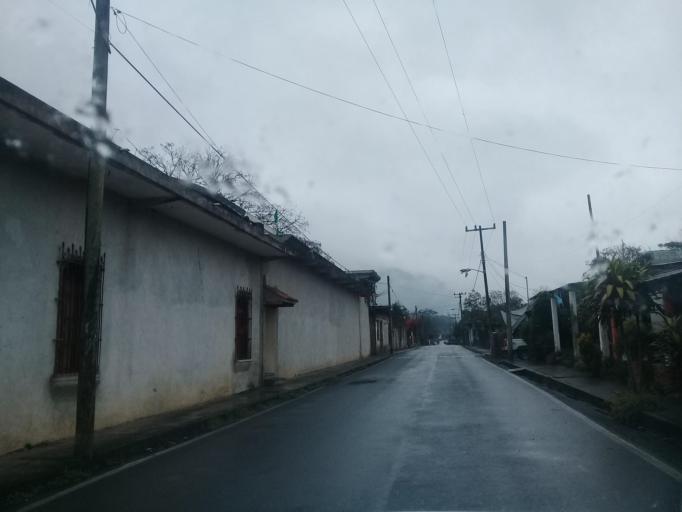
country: MX
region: Veracruz
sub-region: Amatlan de los Reyes
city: Centro de Readaptacion Social
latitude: 18.8063
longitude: -96.9566
